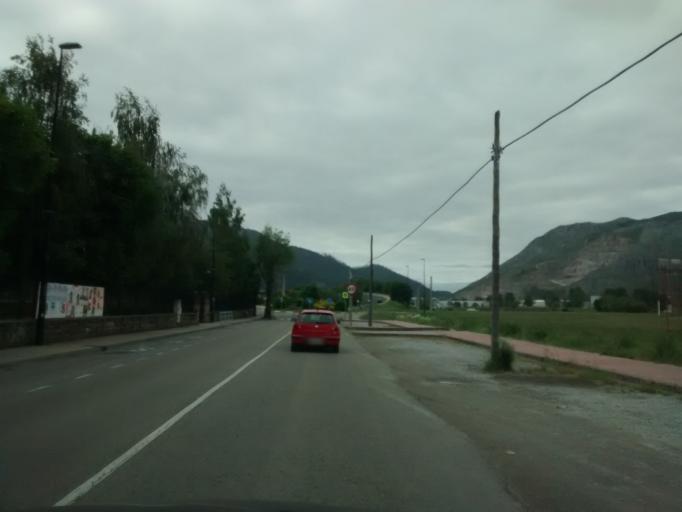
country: ES
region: Cantabria
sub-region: Provincia de Cantabria
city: Los Corrales de Buelna
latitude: 43.2672
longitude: -4.0729
